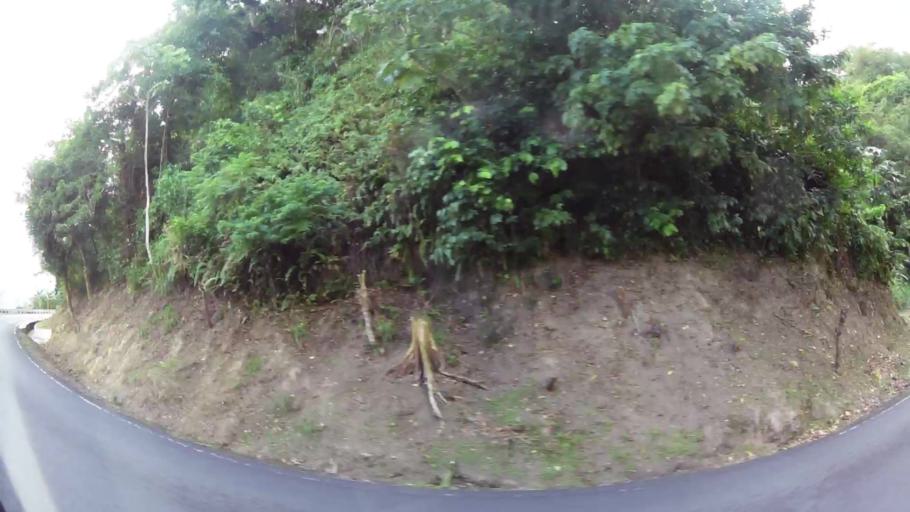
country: LC
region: Dennery Quarter
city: Dennery
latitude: 13.9292
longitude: -60.9432
